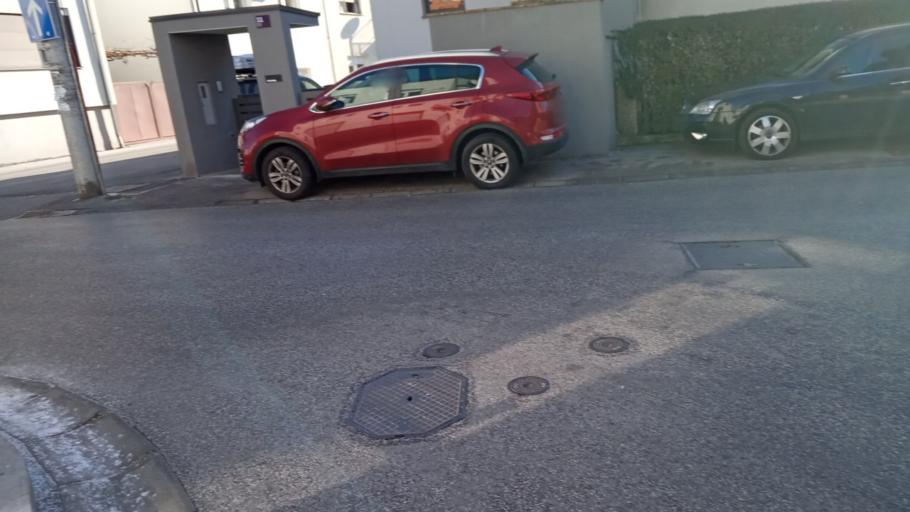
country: HR
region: Grad Zagreb
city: Jankomir
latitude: 45.7926
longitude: 15.9354
